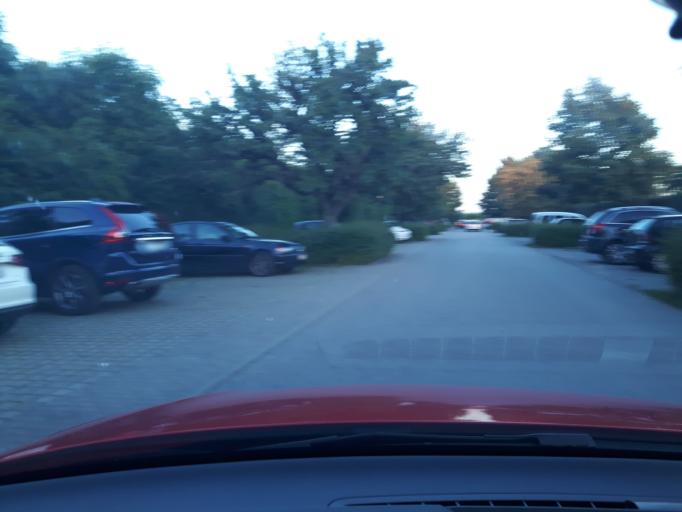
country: DE
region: Baden-Wuerttemberg
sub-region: Regierungsbezirk Stuttgart
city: Cleebronn
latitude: 49.0437
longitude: 9.0479
